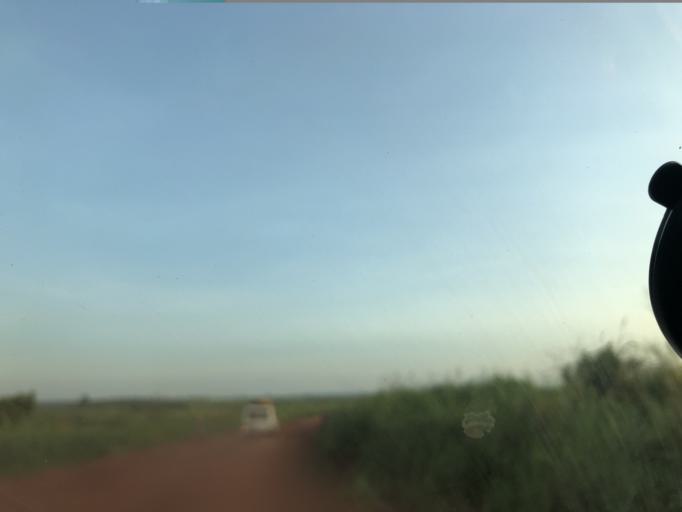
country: CF
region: Bangui
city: Bangui
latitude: 4.1368
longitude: 18.7951
